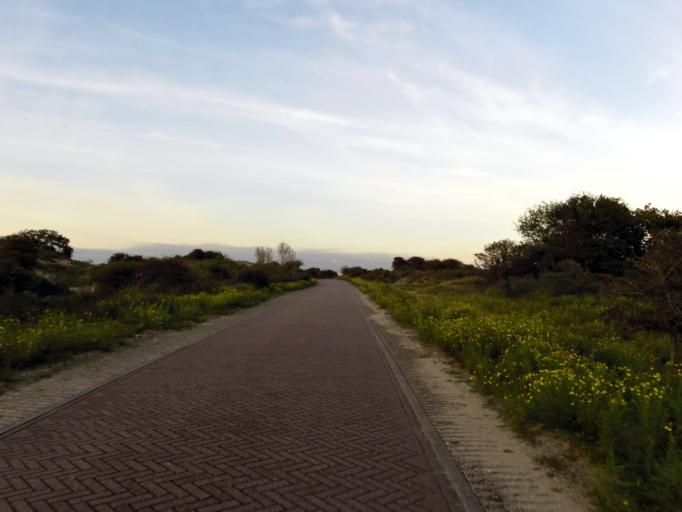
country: NL
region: South Holland
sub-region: Gemeente Wassenaar
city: Wassenaar
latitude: 52.1424
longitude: 4.3423
